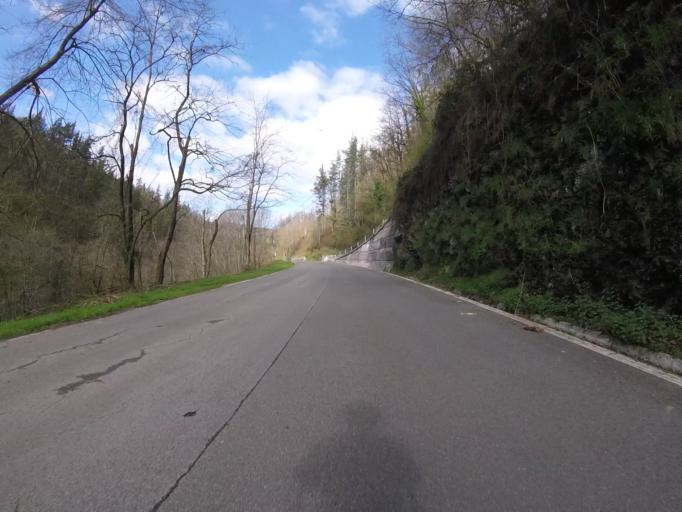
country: ES
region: Navarre
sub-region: Provincia de Navarra
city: Goizueta
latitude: 43.1633
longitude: -1.8525
